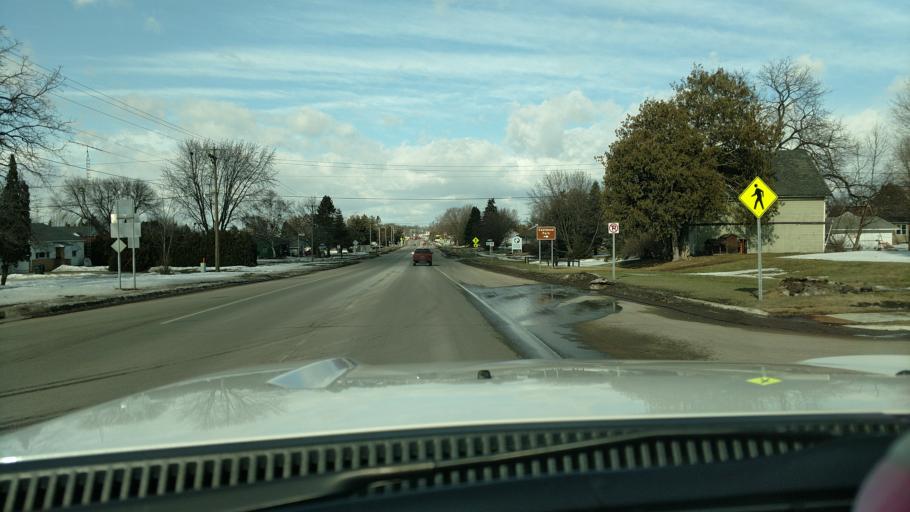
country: US
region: Minnesota
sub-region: Wabasha County
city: Plainview
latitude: 44.1659
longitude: -92.1657
